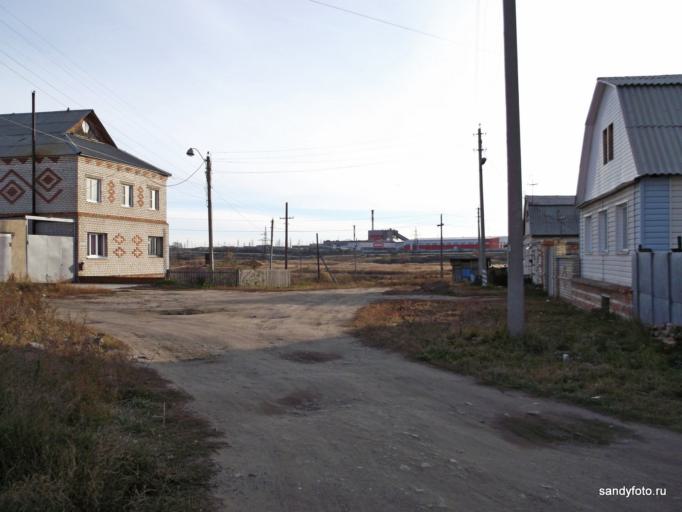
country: RU
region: Chelyabinsk
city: Troitsk
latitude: 54.0728
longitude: 61.5876
